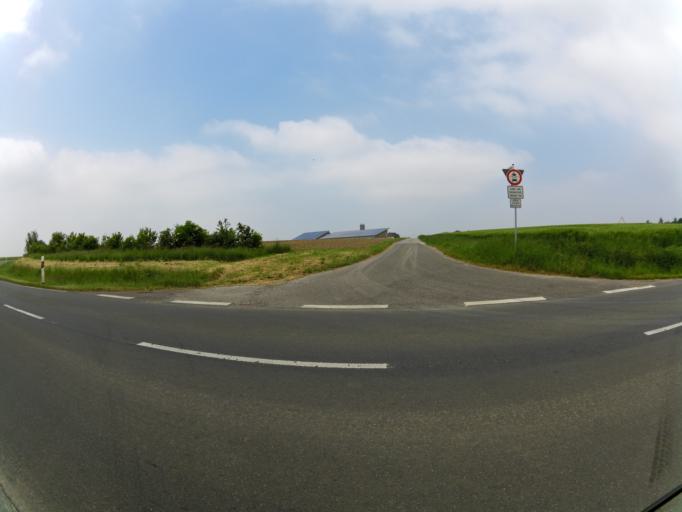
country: DE
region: North Rhine-Westphalia
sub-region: Regierungsbezirk Koln
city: Heinsberg
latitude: 51.0370
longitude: 6.1376
